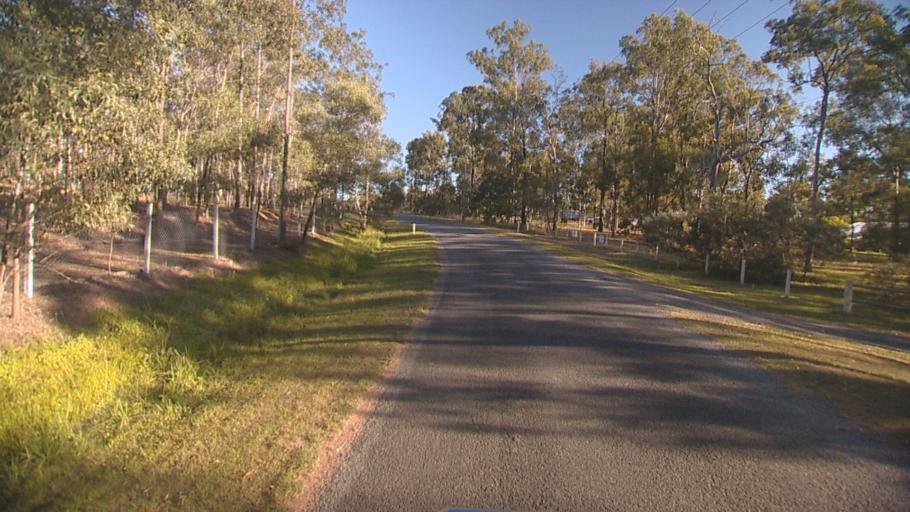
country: AU
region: Queensland
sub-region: Logan
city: North Maclean
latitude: -27.7554
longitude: 153.0209
